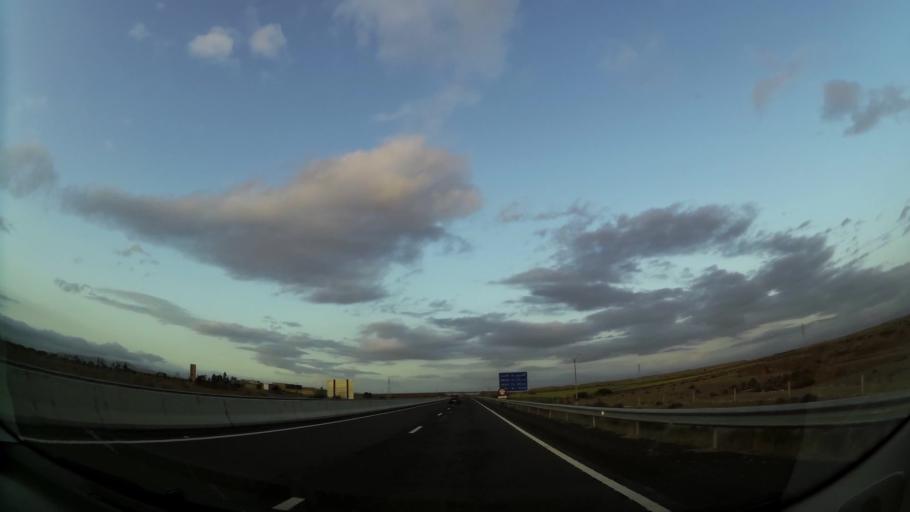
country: MA
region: Oriental
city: Taourirt
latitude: 34.5501
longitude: -2.8682
